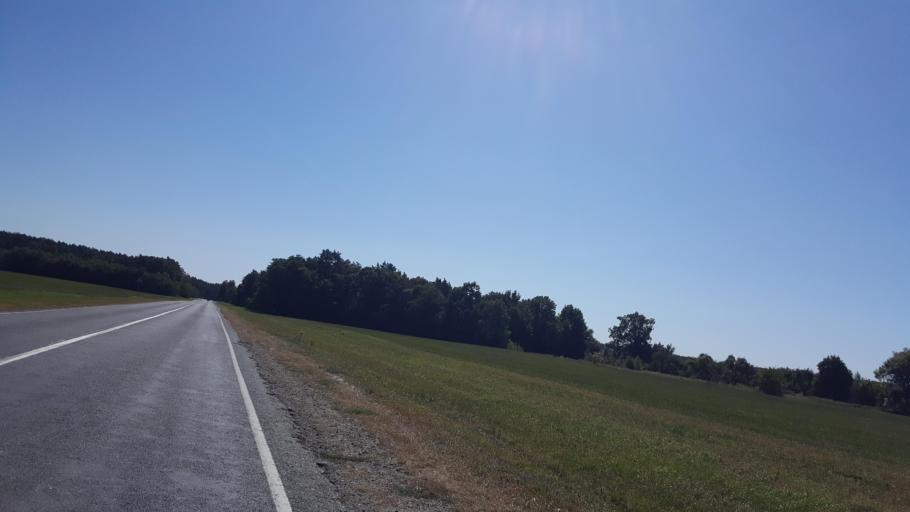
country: BY
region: Brest
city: Vysokaye
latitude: 52.2367
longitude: 23.5012
